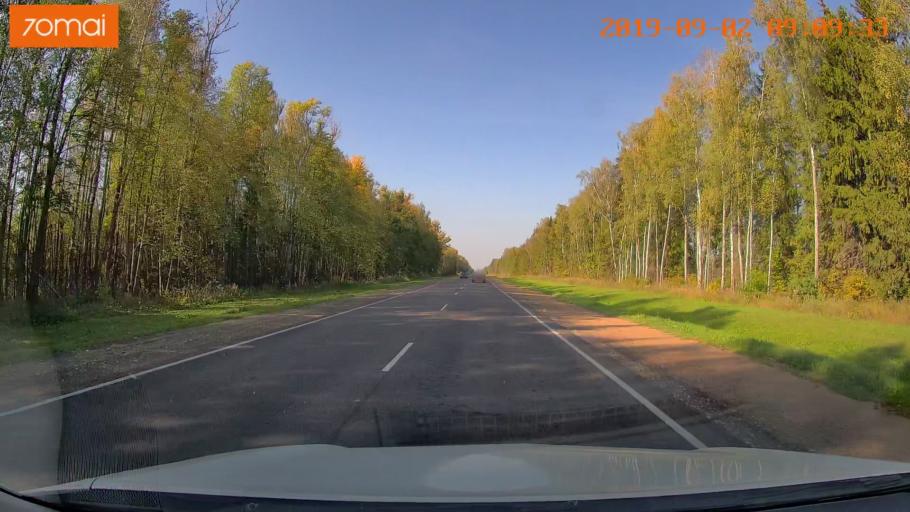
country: RU
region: Kaluga
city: Myatlevo
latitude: 54.8834
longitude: 35.6218
